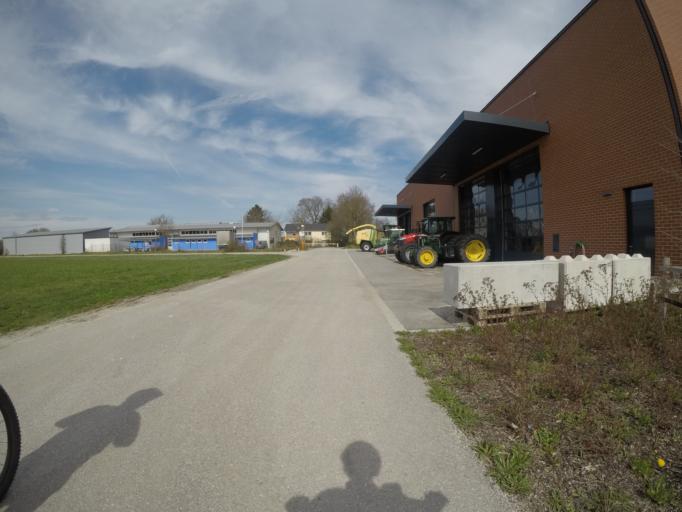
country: DE
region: Bavaria
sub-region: Lower Bavaria
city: Stallwang
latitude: 48.5602
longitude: 12.1998
